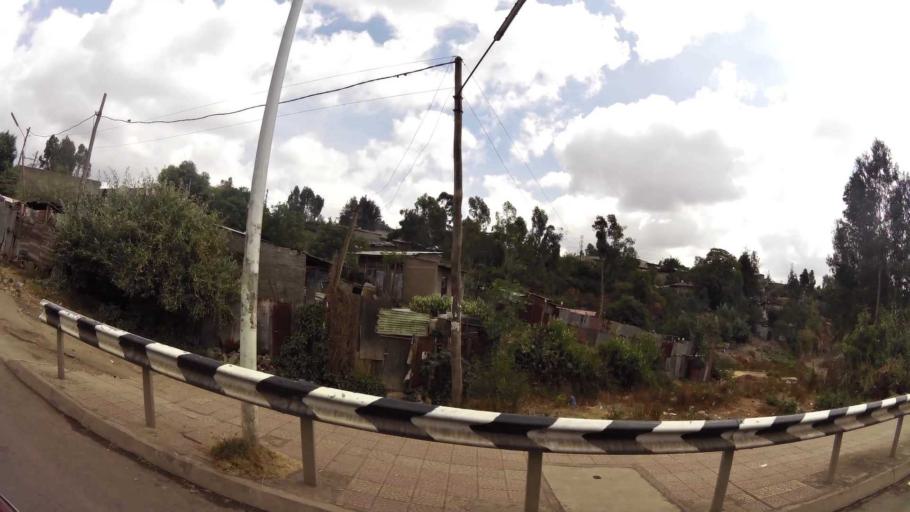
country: ET
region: Adis Abeba
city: Addis Ababa
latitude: 8.9503
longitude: 38.7592
